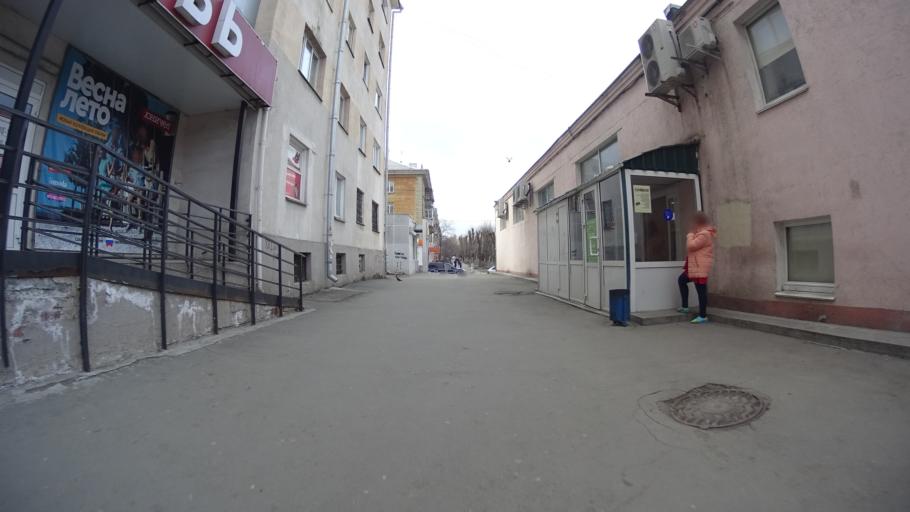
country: RU
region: Chelyabinsk
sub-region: Gorod Chelyabinsk
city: Chelyabinsk
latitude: 55.1617
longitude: 61.4409
